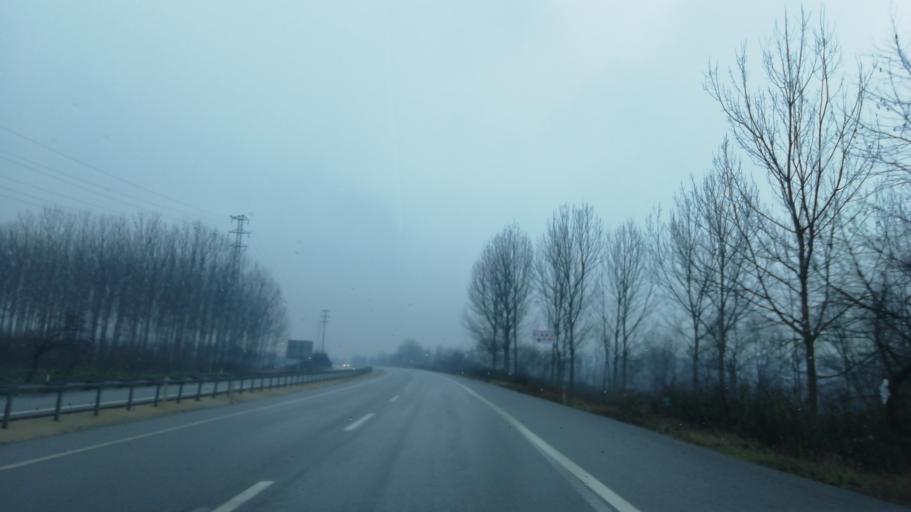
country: TR
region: Sakarya
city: Akyazi
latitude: 40.6571
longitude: 30.5979
